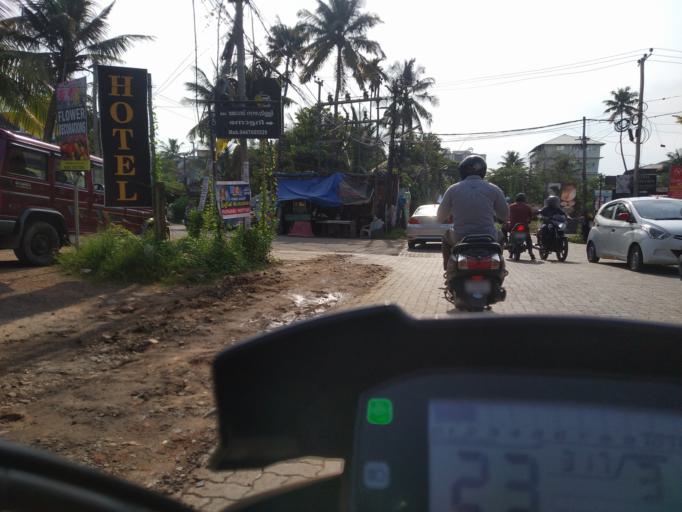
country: IN
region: Kerala
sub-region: Ernakulam
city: Cochin
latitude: 9.9834
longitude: 76.3006
